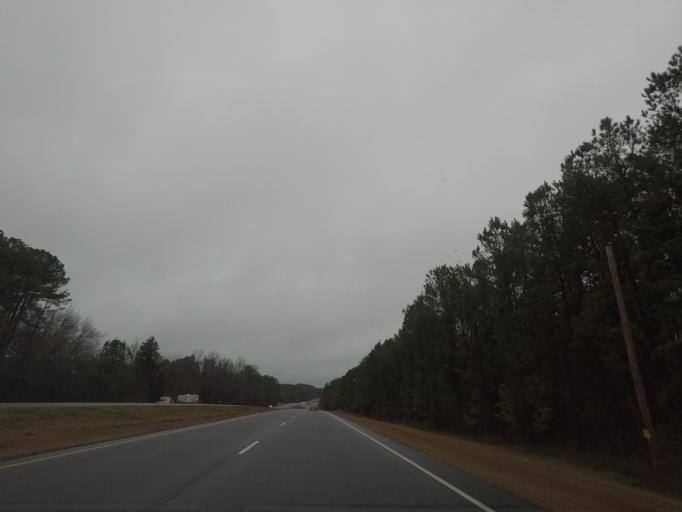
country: US
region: North Carolina
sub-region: Lee County
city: Broadway
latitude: 35.3220
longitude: -79.0915
